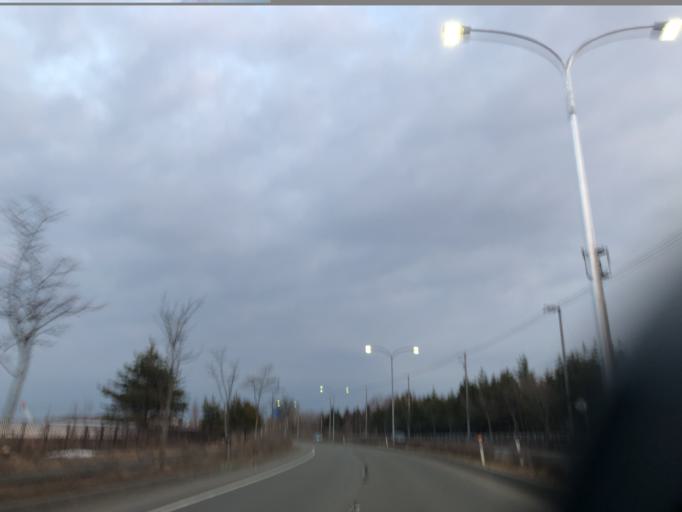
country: JP
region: Hokkaido
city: Chitose
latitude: 42.8222
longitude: 141.6720
